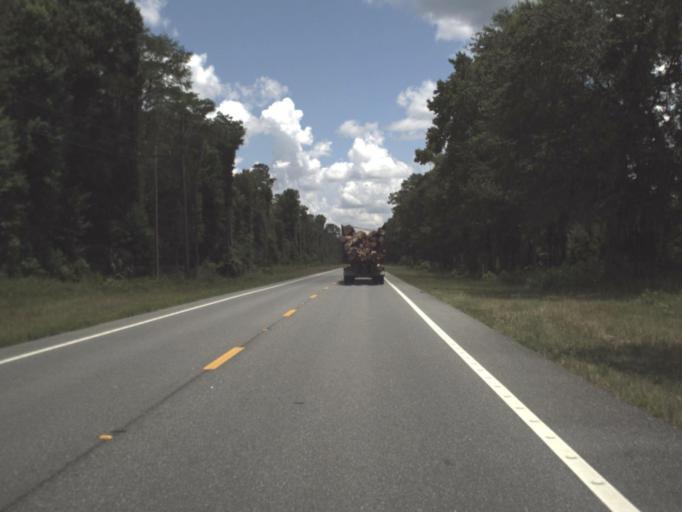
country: US
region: Florida
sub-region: Taylor County
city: Perry
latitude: 30.1428
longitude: -83.8212
